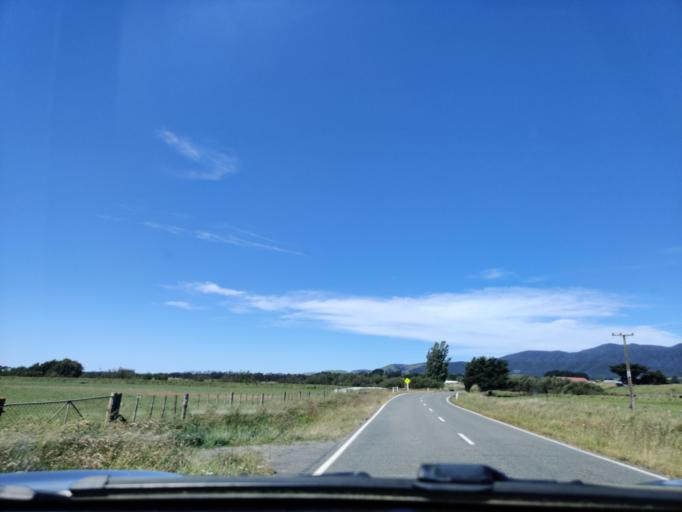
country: NZ
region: Wellington
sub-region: Upper Hutt City
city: Upper Hutt
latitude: -41.3278
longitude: 175.2175
